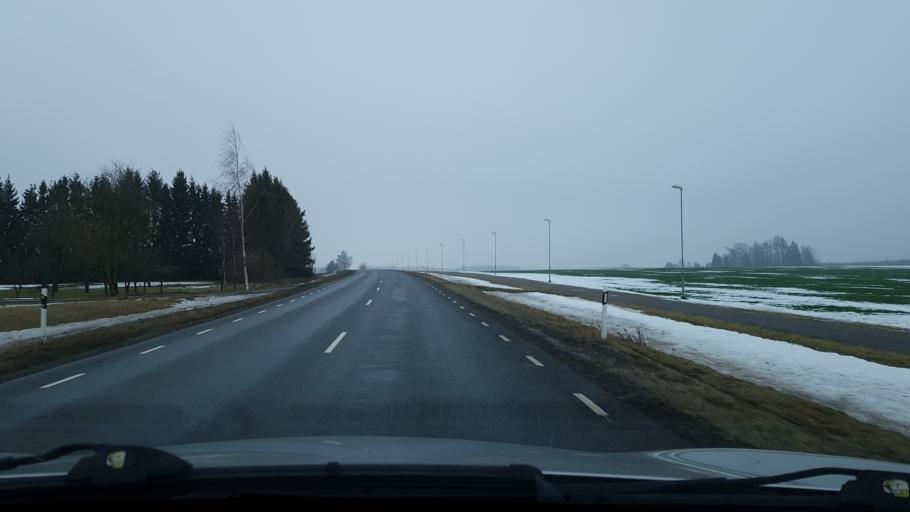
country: EE
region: Valgamaa
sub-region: Torva linn
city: Torva
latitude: 58.2215
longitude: 25.8972
